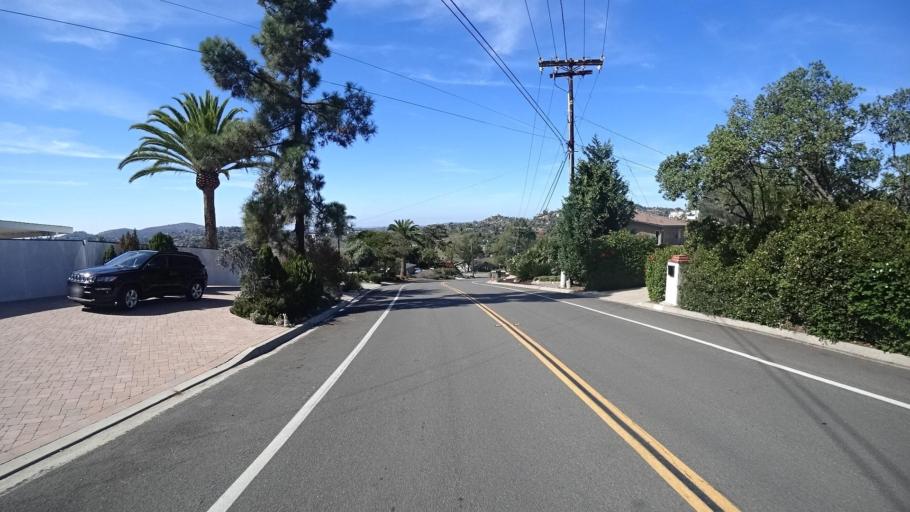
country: US
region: California
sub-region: San Diego County
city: Casa de Oro-Mount Helix
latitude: 32.7568
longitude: -116.9538
